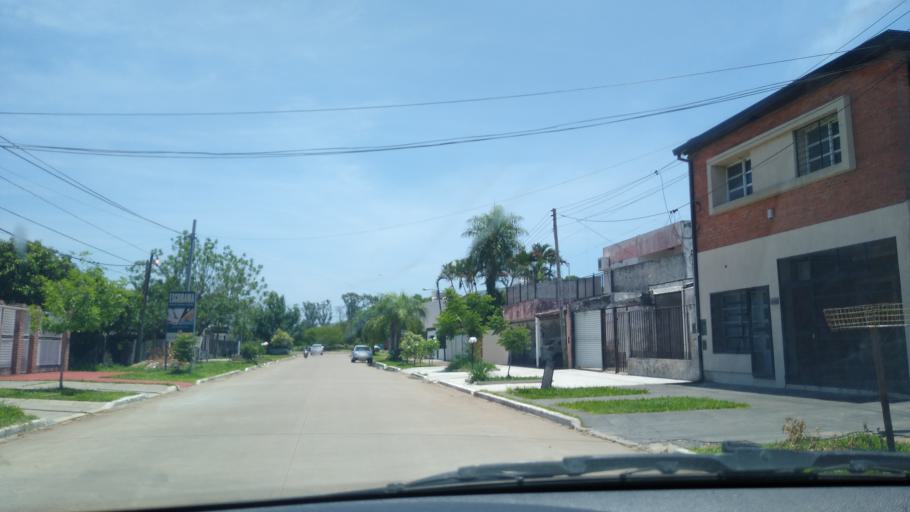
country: AR
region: Chaco
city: Barranqueras
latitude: -27.4853
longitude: -58.9515
